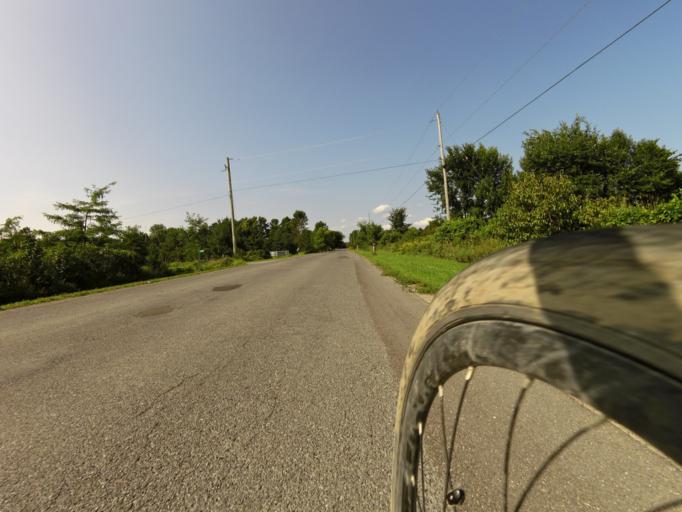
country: CA
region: Ontario
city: Kingston
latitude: 44.3206
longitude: -76.6724
